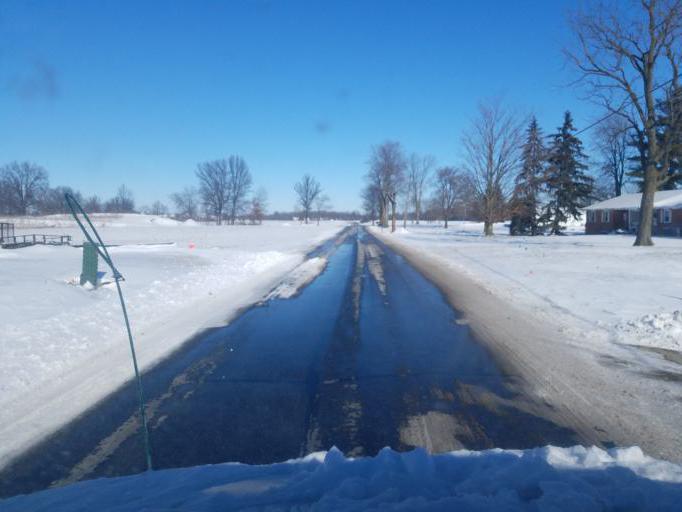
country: US
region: Ohio
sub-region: Delaware County
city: Delaware
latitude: 40.2839
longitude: -83.0307
